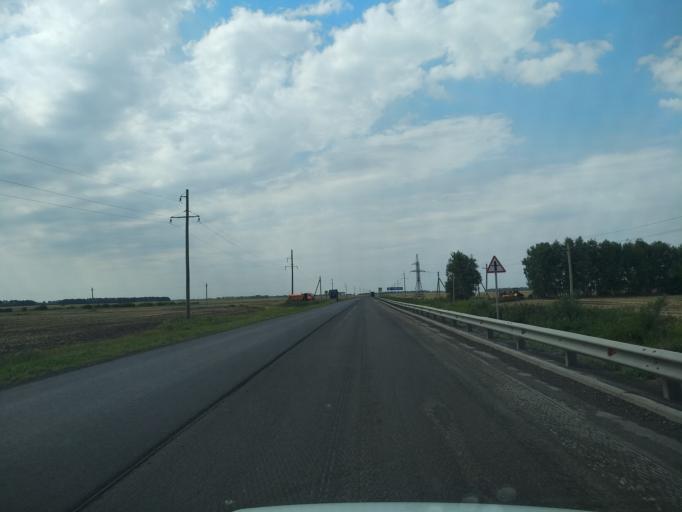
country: RU
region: Voronezj
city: Pereleshino
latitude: 51.7940
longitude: 40.1483
